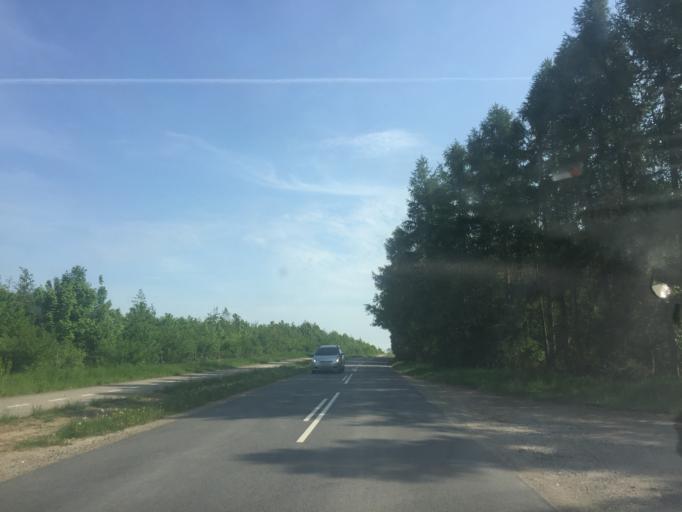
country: DK
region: Capital Region
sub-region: Egedal Kommune
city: Smorumnedre
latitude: 55.7249
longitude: 12.2913
